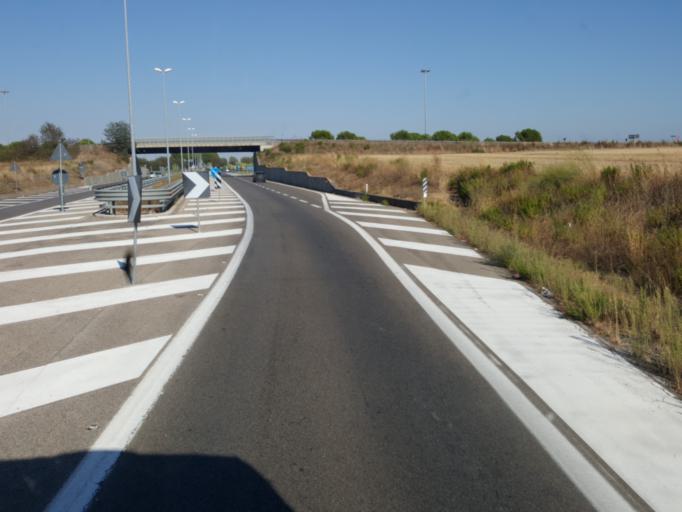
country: IT
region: Tuscany
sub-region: Provincia di Grosseto
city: Capalbio
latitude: 42.4147
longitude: 11.4078
